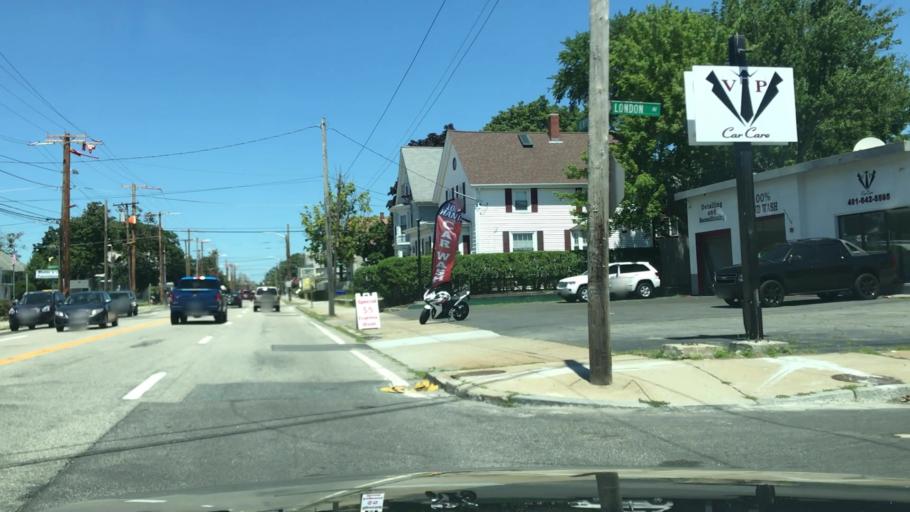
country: US
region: Massachusetts
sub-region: Bristol County
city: North Seekonk
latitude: 41.8843
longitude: -71.3541
